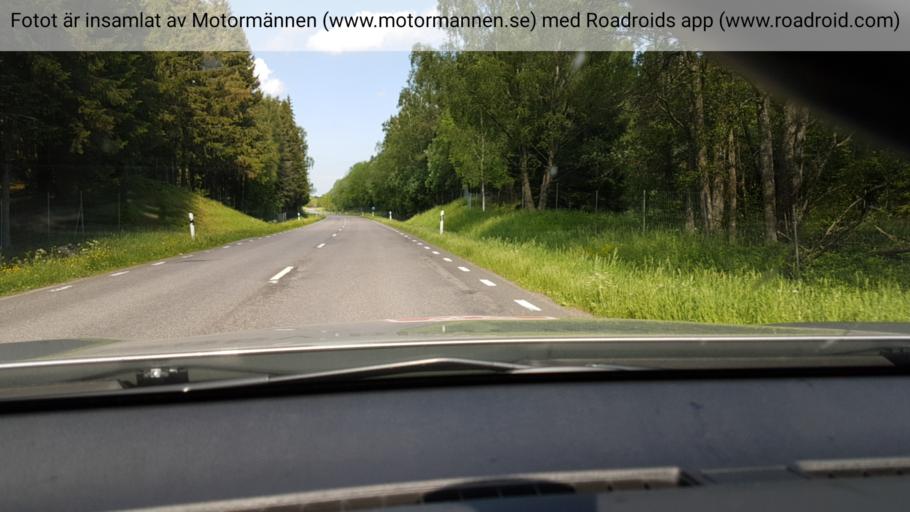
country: SE
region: Vaestra Goetaland
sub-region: Falkopings Kommun
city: Falkoeping
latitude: 58.0606
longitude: 13.5397
